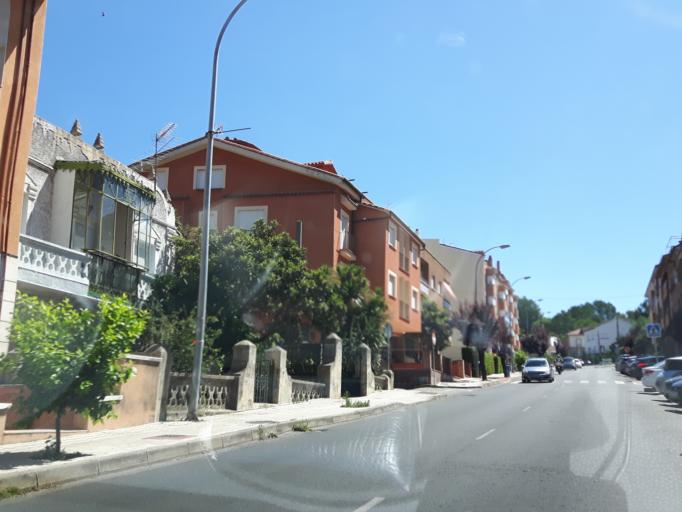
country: ES
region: Castille and Leon
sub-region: Provincia de Avila
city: Arenas de San Pedro
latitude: 40.2107
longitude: -5.0841
